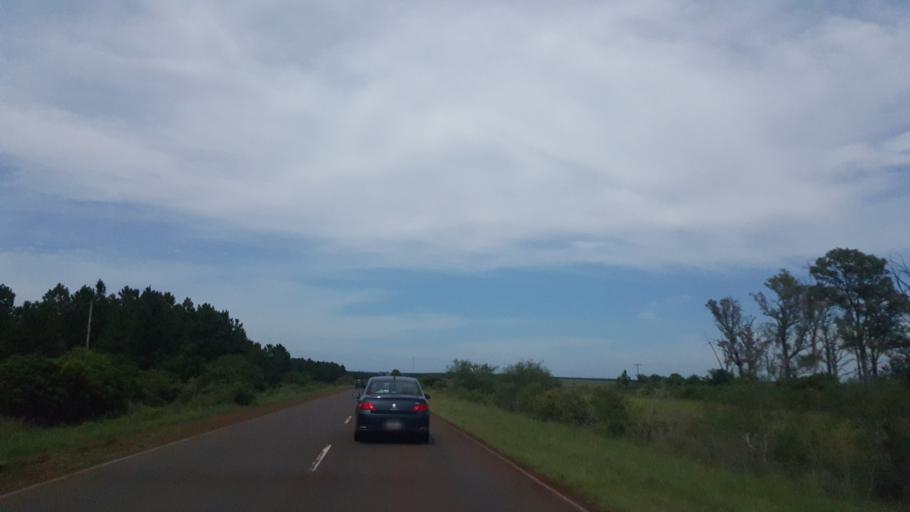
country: PY
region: Itapua
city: San Juan del Parana
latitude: -27.5067
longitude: -56.1272
